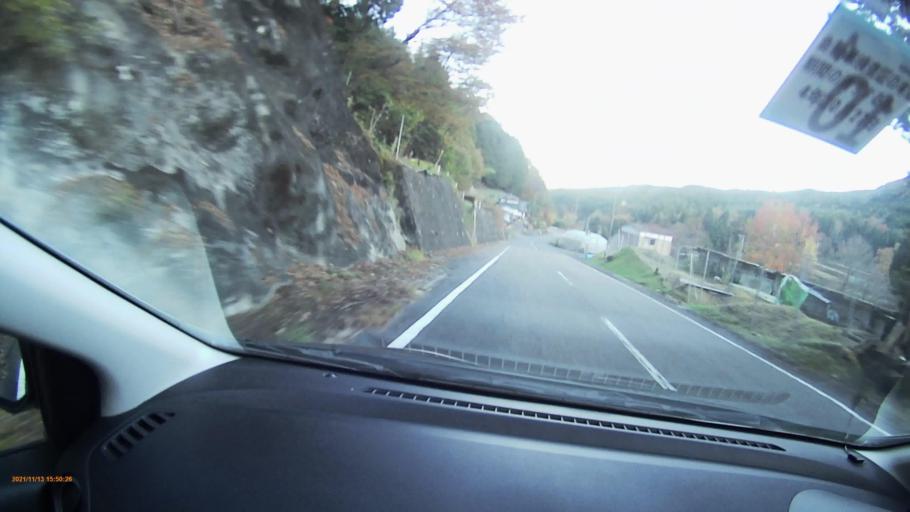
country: JP
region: Gifu
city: Nakatsugawa
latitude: 35.5972
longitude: 137.4112
